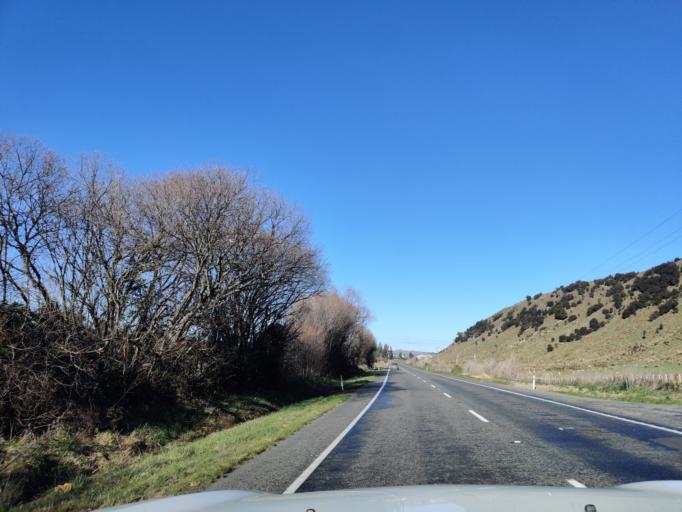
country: NZ
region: Manawatu-Wanganui
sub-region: Ruapehu District
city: Waiouru
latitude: -39.8416
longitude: 175.7419
